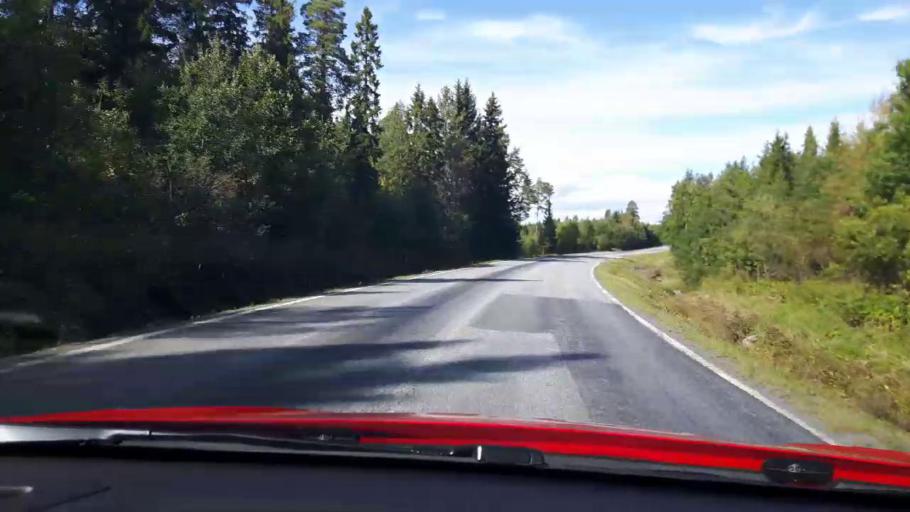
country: SE
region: Jaemtland
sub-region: OEstersunds Kommun
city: Ostersund
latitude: 63.0730
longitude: 14.4448
